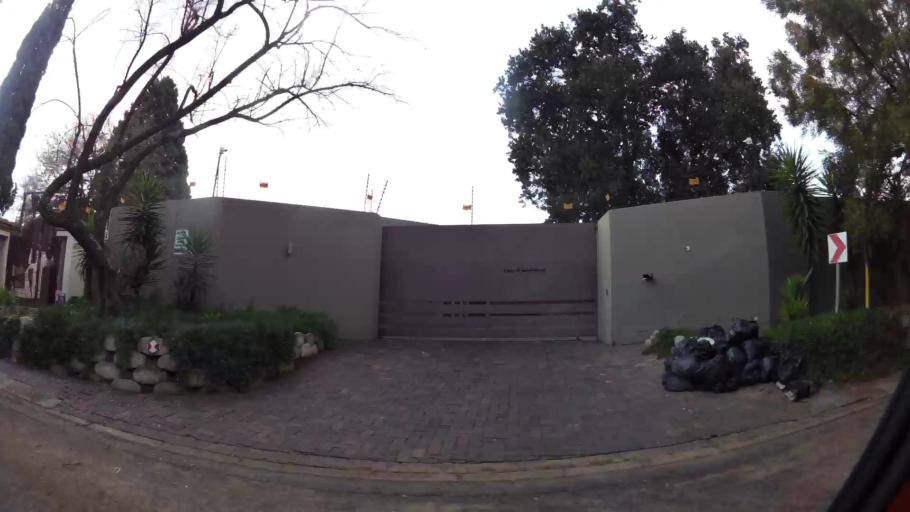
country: ZA
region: Gauteng
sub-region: Sedibeng District Municipality
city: Vanderbijlpark
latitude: -26.7435
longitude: 27.8286
